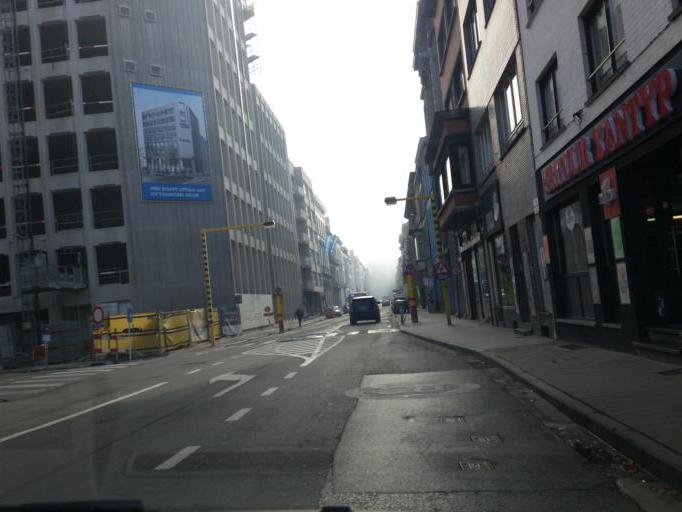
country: BE
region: Flanders
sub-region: Provincie Oost-Vlaanderen
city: Gent
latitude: 51.0535
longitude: 3.7312
